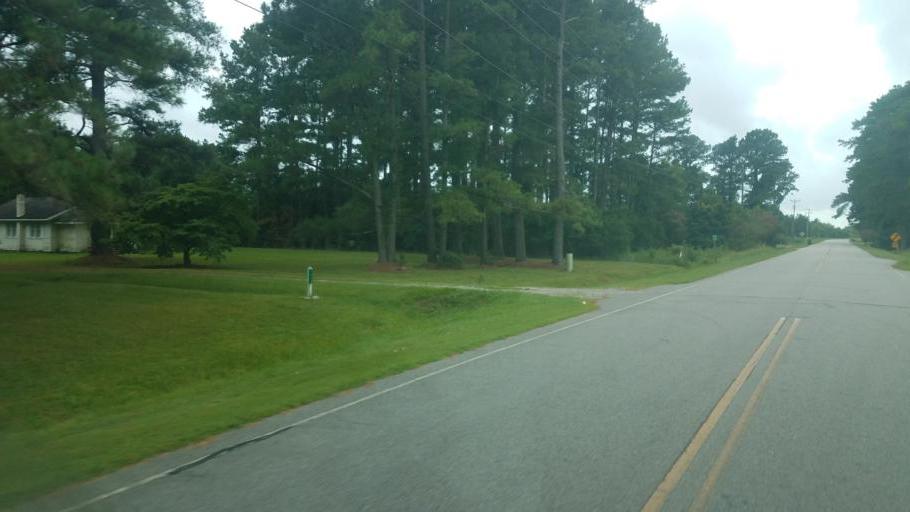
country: US
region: North Carolina
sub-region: Tyrrell County
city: Columbia
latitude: 35.9063
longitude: -76.3111
